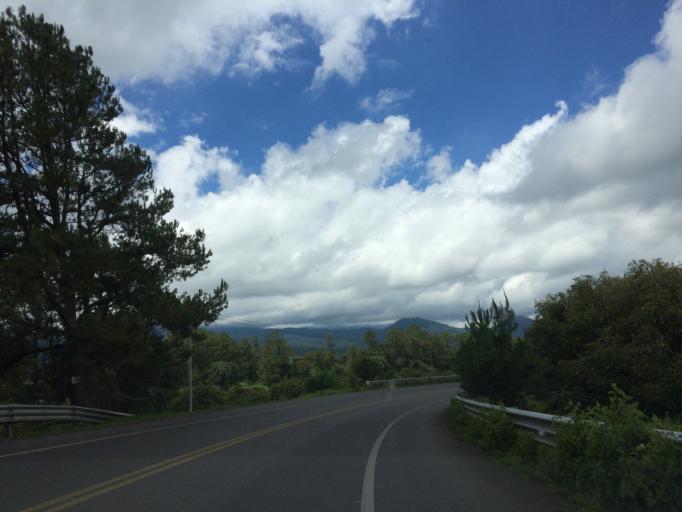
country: MX
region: Michoacan
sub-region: Uruapan
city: Santa Ana Zirosto
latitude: 19.5527
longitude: -102.3003
